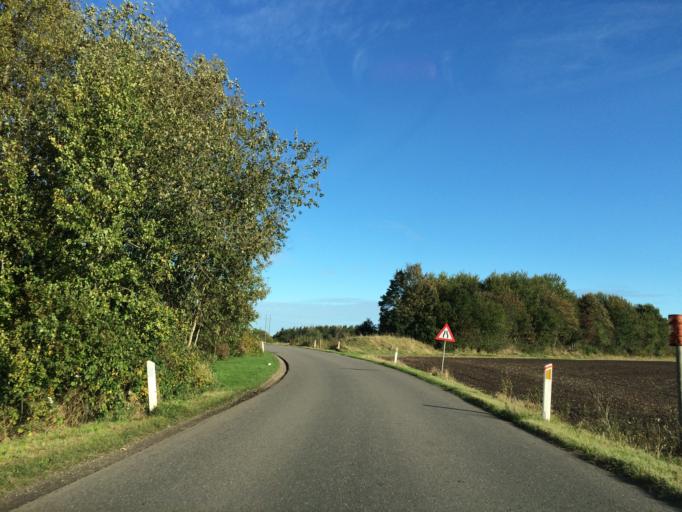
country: DK
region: Central Jutland
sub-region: Favrskov Kommune
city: Hammel
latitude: 56.2899
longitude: 9.7674
